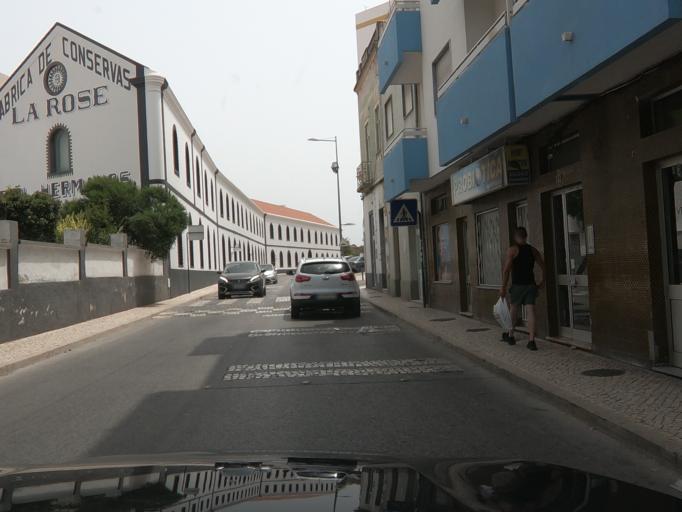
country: PT
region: Faro
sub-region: Portimao
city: Portimao
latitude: 37.1312
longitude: -8.5354
